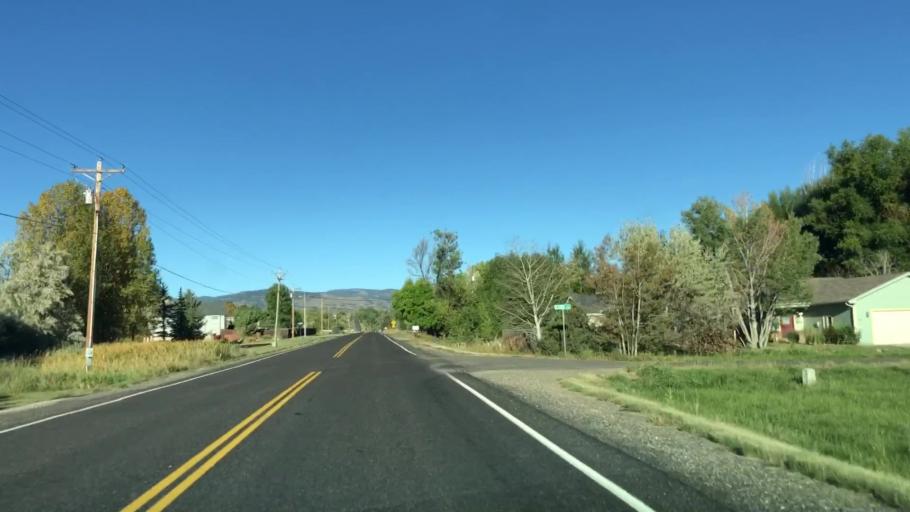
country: US
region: Colorado
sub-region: Larimer County
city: Loveland
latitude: 40.3784
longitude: -105.1369
